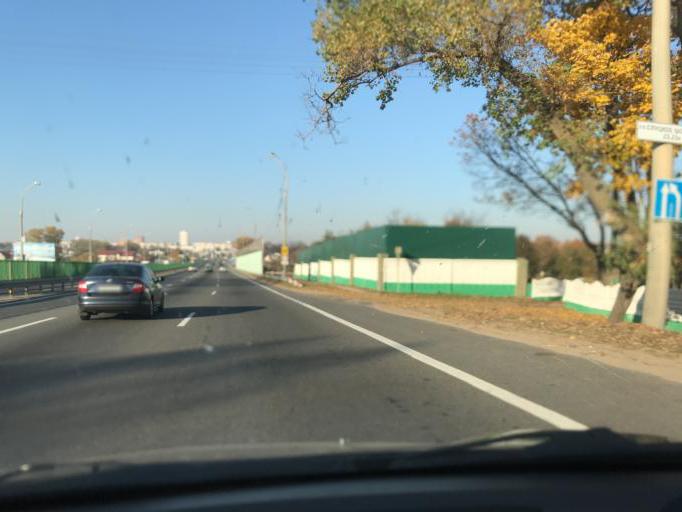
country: BY
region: Minsk
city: Syenitsa
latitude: 53.8270
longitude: 27.5342
